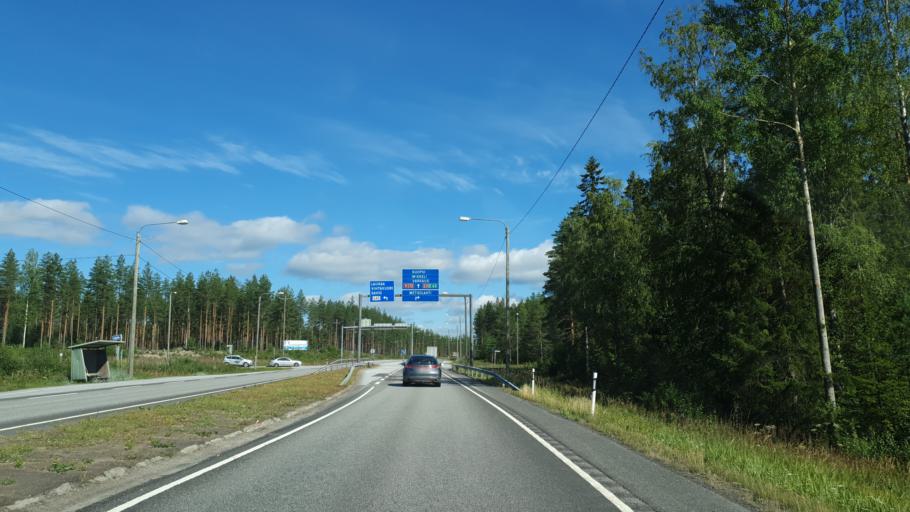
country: FI
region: Central Finland
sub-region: Jyvaeskylae
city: Toivakka
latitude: 62.2528
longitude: 26.0978
